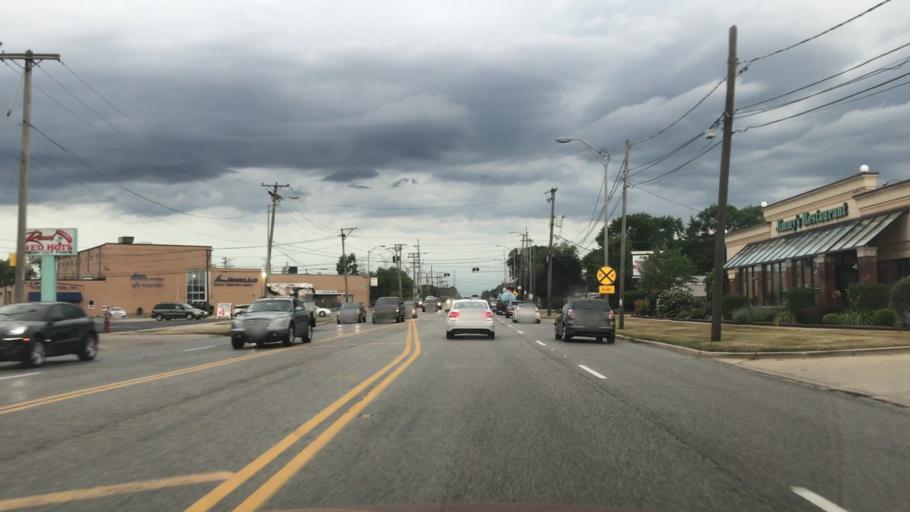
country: US
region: Illinois
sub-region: Cook County
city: Des Plaines
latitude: 42.0489
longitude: -87.8882
